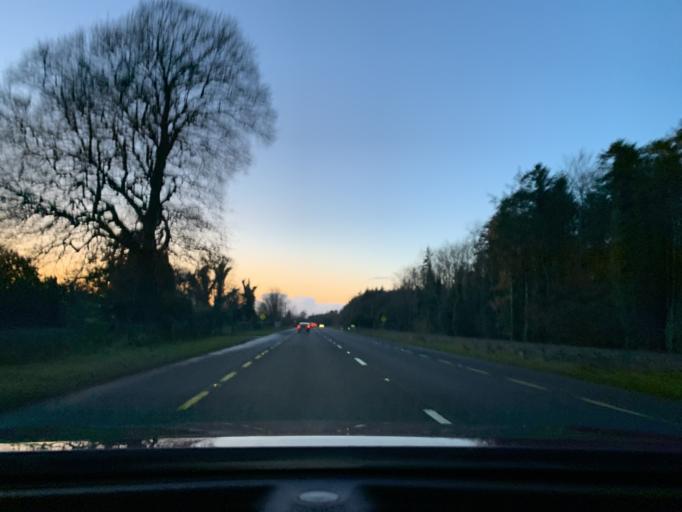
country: IE
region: Connaught
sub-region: Roscommon
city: Boyle
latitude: 53.9693
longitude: -8.2326
